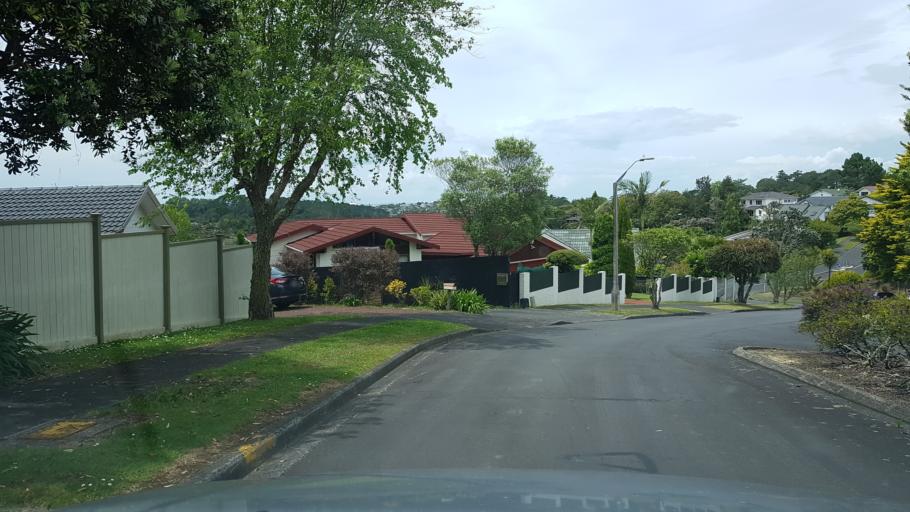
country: NZ
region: Auckland
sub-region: Auckland
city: North Shore
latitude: -36.8197
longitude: 174.7100
